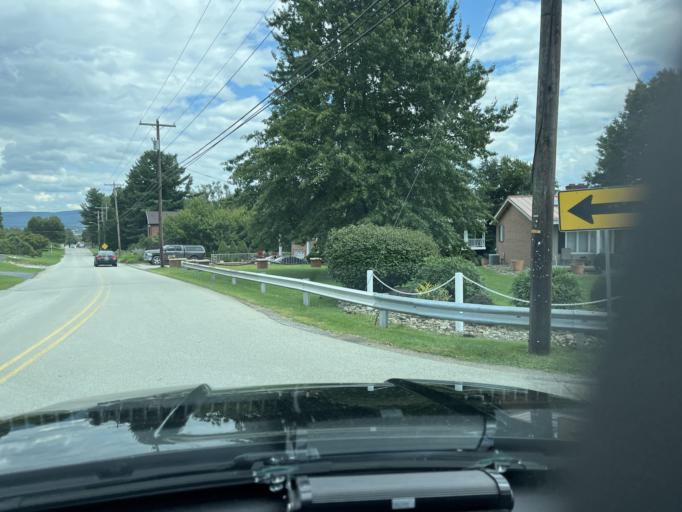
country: US
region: Pennsylvania
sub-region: Fayette County
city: South Uniontown
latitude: 39.8959
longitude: -79.7568
